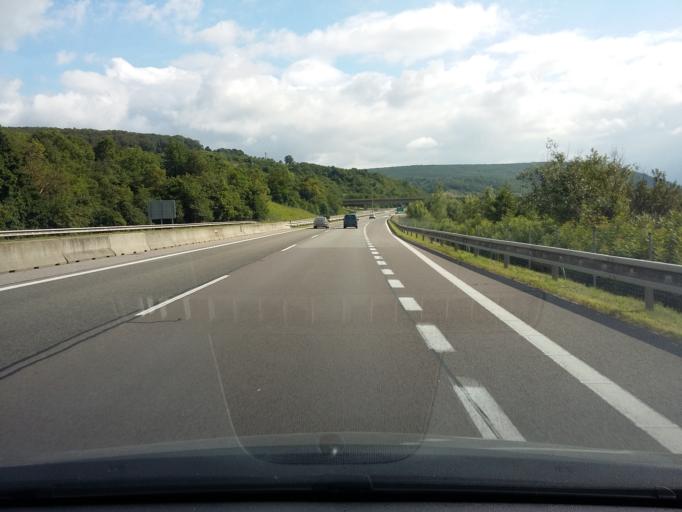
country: SK
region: Trenciansky
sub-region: Okres Trencin
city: Trencin
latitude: 48.9015
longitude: 17.9873
